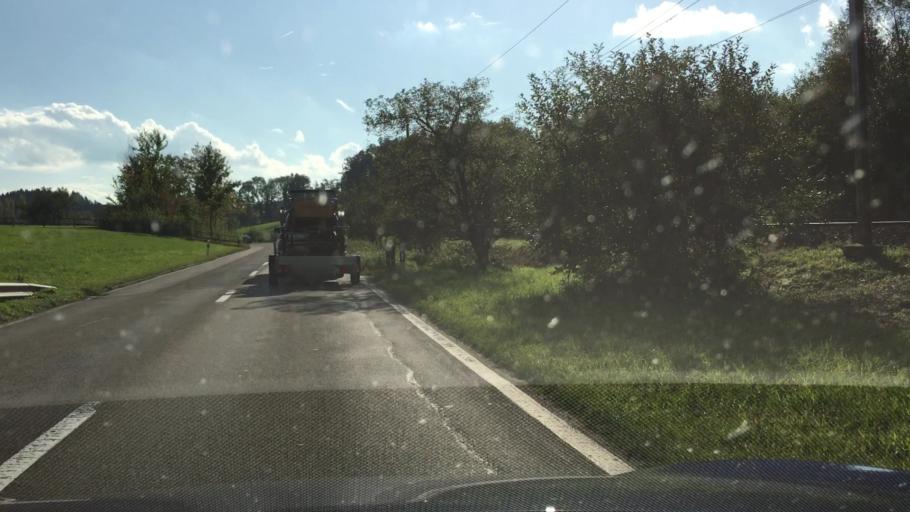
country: CH
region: Saint Gallen
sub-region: Wahlkreis St. Gallen
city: Waldkirch
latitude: 47.4642
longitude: 9.2488
